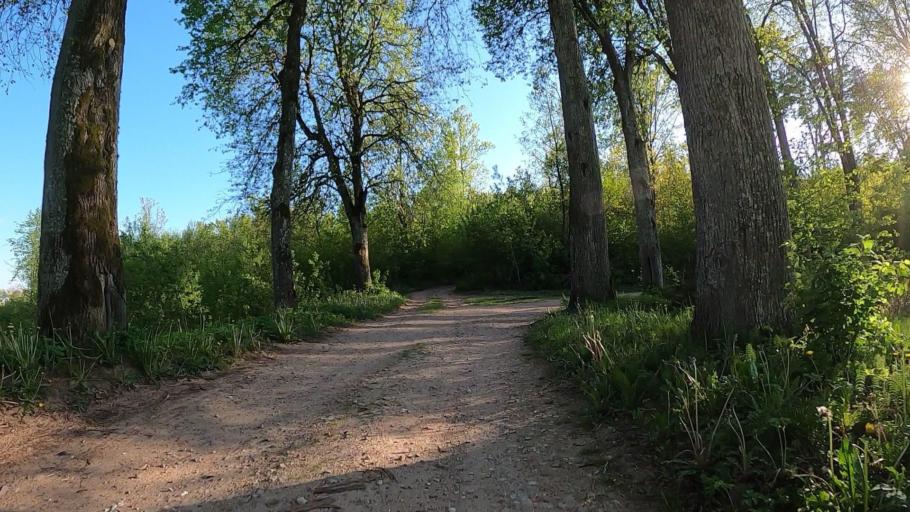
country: LV
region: Kekava
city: Kekava
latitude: 56.7774
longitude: 24.2948
